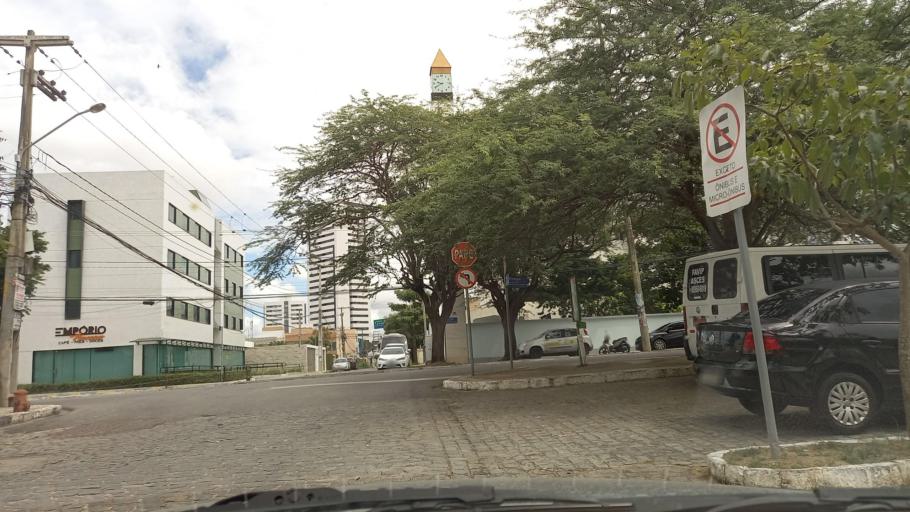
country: BR
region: Pernambuco
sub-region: Caruaru
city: Caruaru
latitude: -8.2687
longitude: -35.9639
